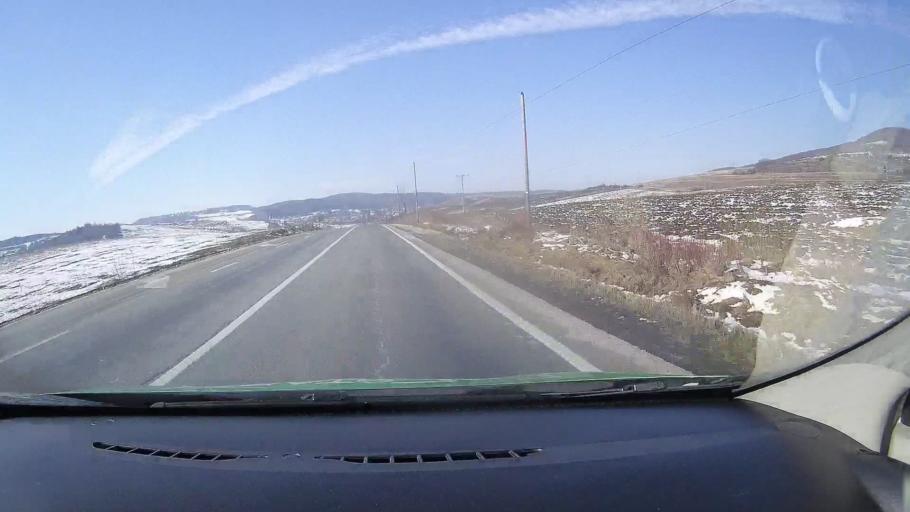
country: RO
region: Brasov
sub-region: Comuna Bunesti
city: Bunesti
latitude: 46.1134
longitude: 25.0433
